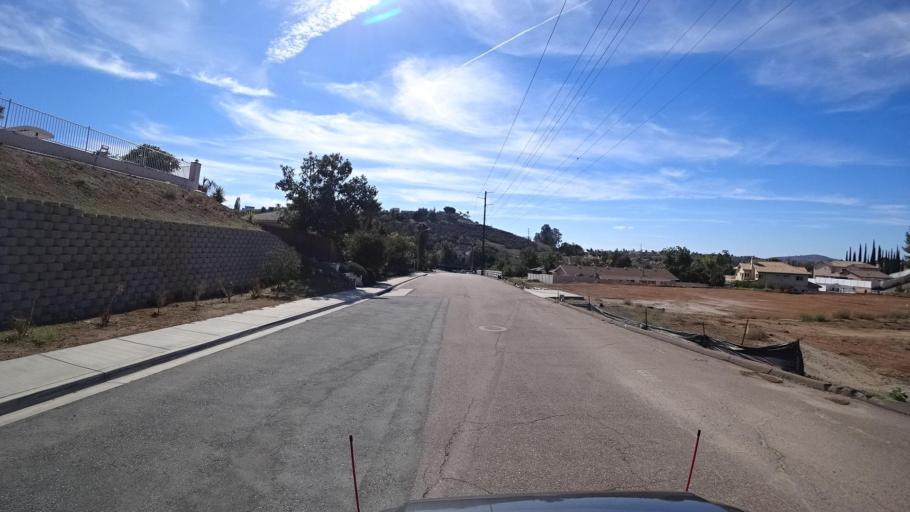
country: US
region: California
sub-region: San Diego County
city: Casa de Oro-Mount Helix
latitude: 32.7529
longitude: -116.9535
